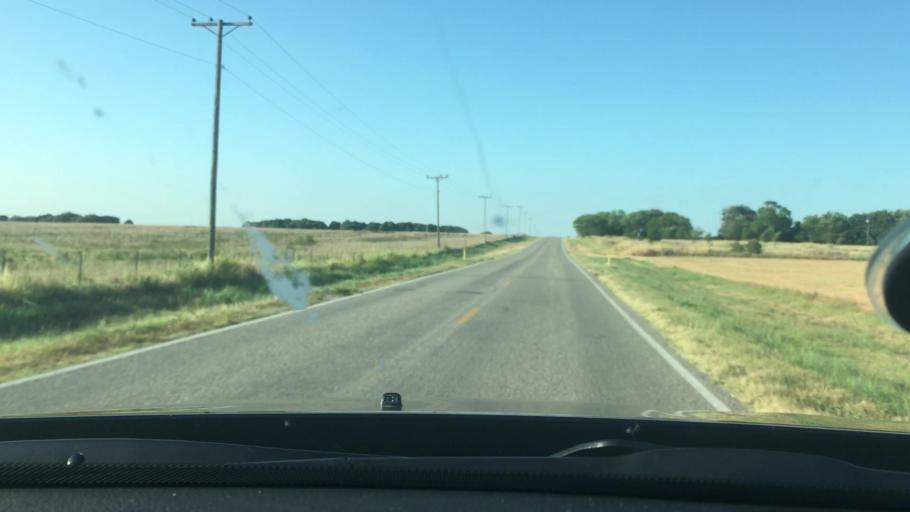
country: US
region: Oklahoma
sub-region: Murray County
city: Sulphur
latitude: 34.5763
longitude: -96.8448
